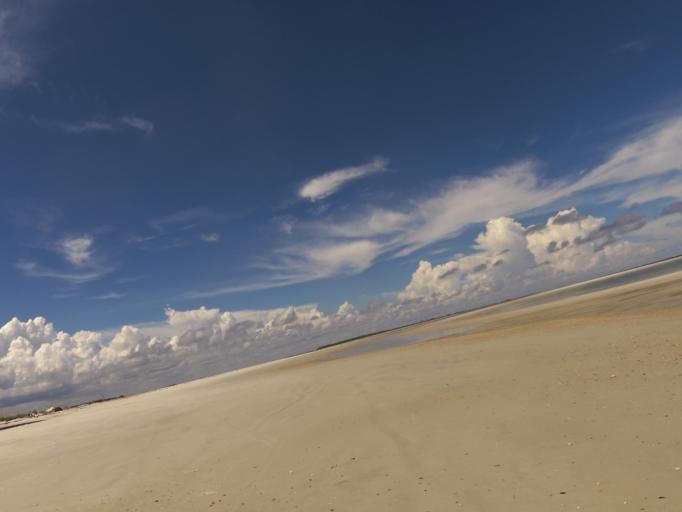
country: US
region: Florida
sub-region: Duval County
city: Atlantic Beach
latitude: 30.4843
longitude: -81.4149
